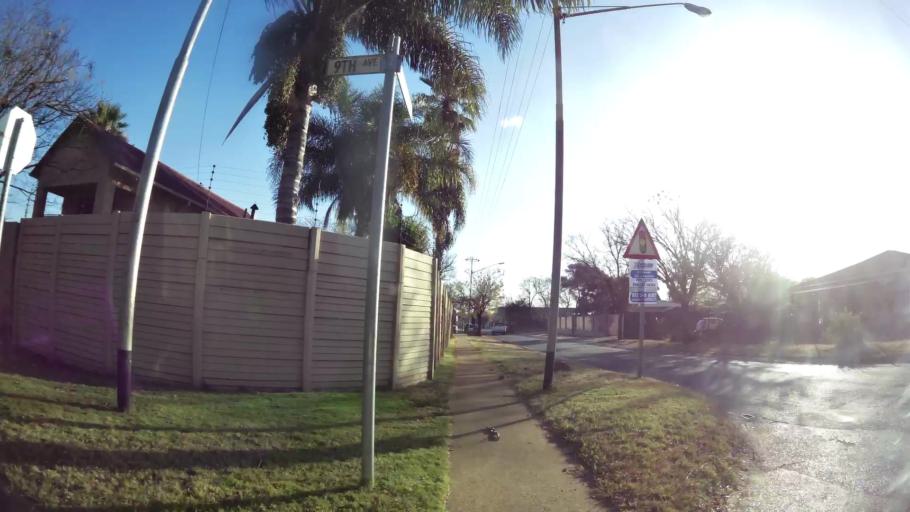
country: ZA
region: Gauteng
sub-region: City of Tshwane Metropolitan Municipality
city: Pretoria
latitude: -25.7051
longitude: 28.2018
